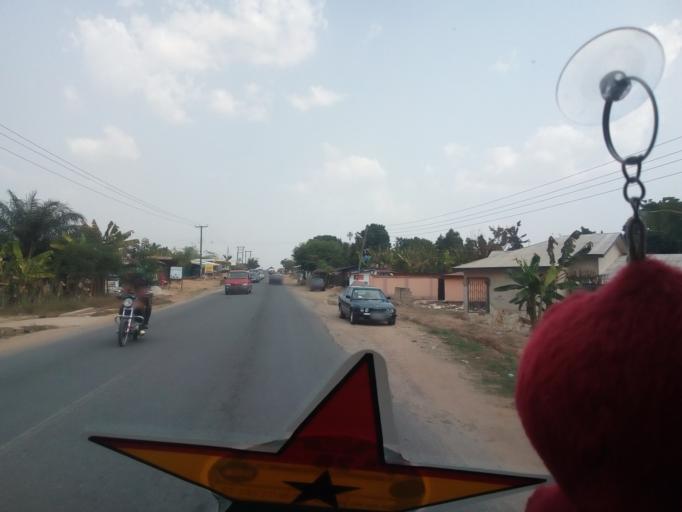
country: GH
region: Eastern
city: Suhum
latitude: 6.0422
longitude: -0.4375
